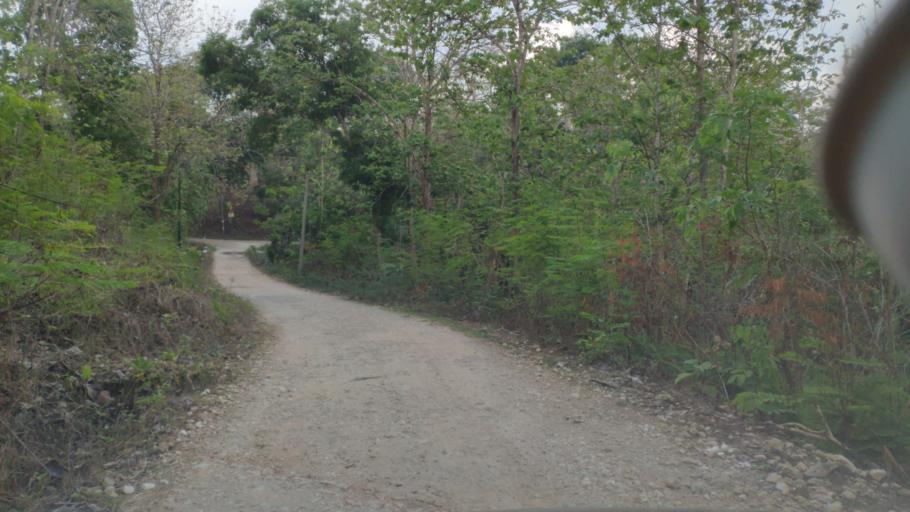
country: ID
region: Central Java
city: Semanggi
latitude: -7.0666
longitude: 111.4314
